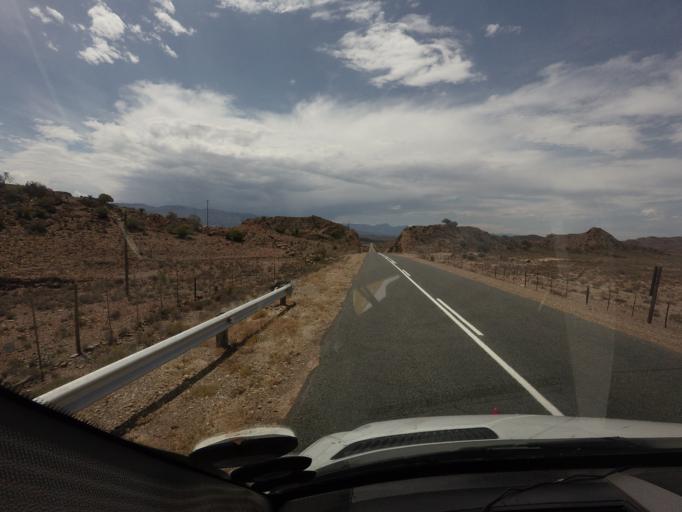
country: ZA
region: Western Cape
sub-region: Eden District Municipality
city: Ladismith
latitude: -33.6910
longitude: 20.9691
